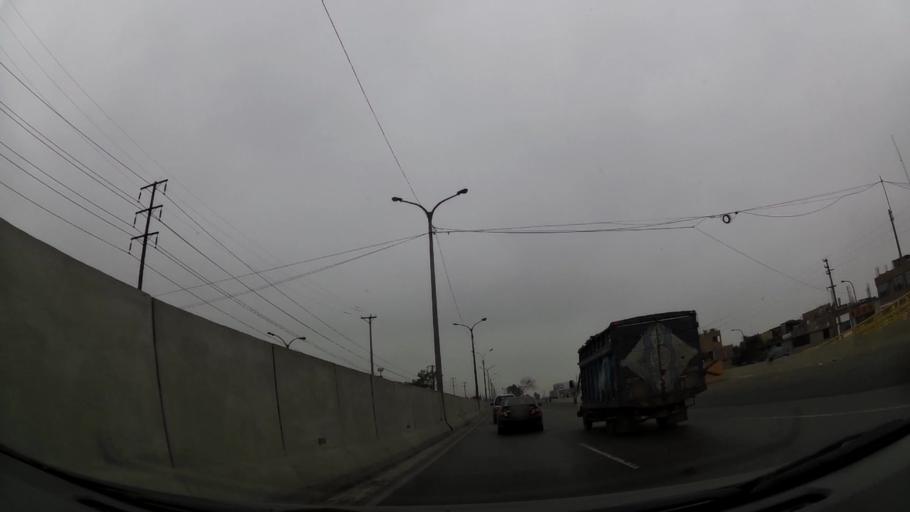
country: PE
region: Lima
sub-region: Lima
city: Urb. Santo Domingo
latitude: -11.9228
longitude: -77.0732
